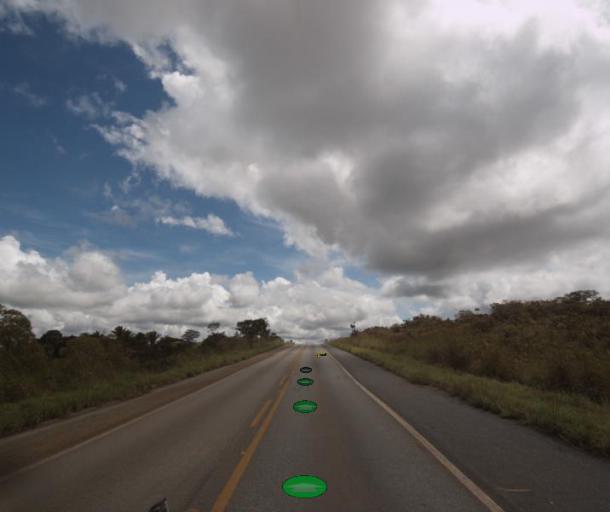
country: BR
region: Goias
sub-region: Pirenopolis
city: Pirenopolis
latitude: -15.7761
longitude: -48.5027
